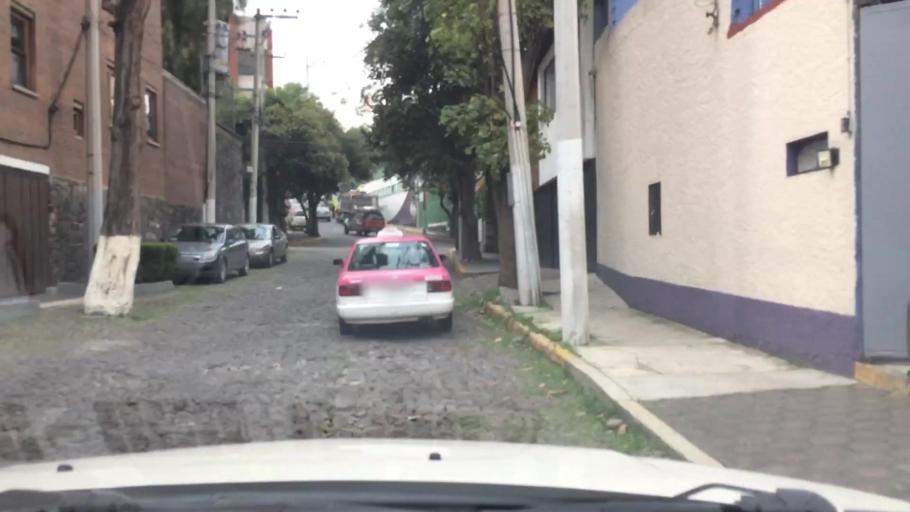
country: MX
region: Mexico City
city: Alvaro Obregon
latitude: 19.3535
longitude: -99.2015
